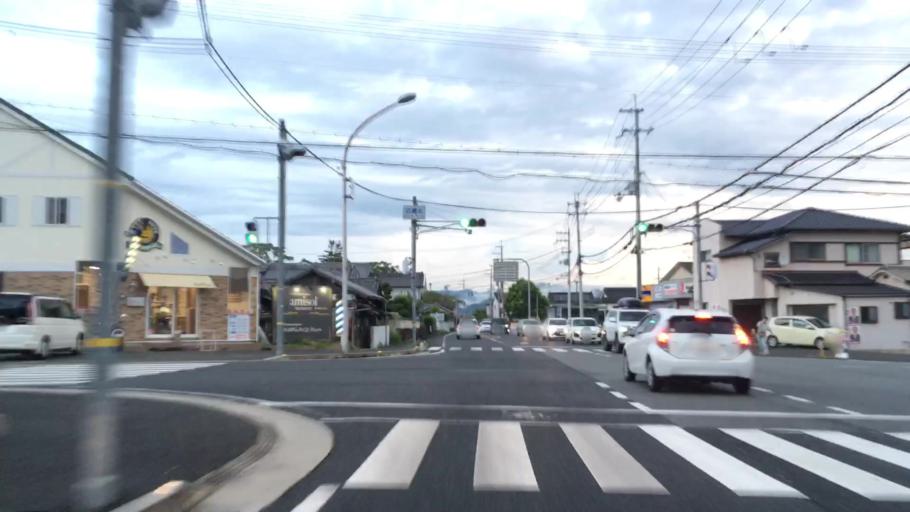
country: JP
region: Hyogo
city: Himeji
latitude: 34.9143
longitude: 134.7401
